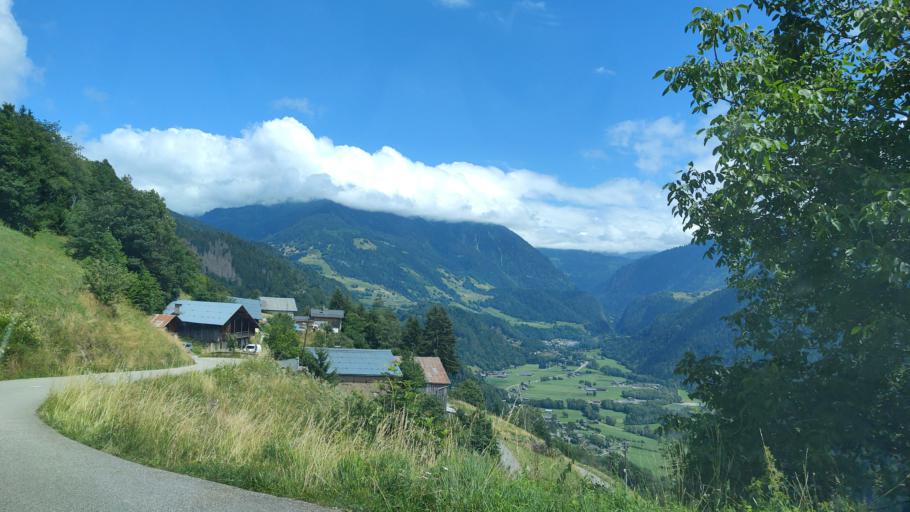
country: FR
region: Rhone-Alpes
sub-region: Departement de la Savoie
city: Beaufort
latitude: 45.7309
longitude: 6.5190
